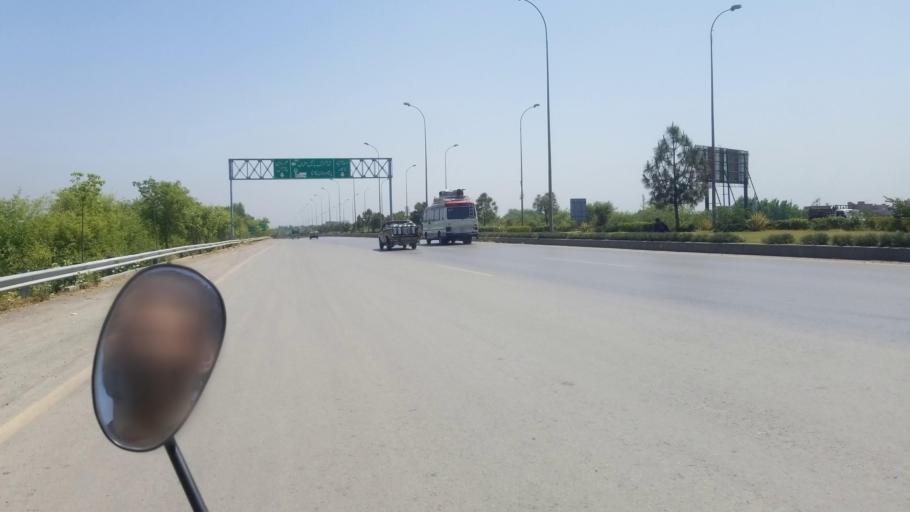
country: PK
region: Khyber Pakhtunkhwa
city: Peshawar
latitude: 34.0274
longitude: 71.6505
